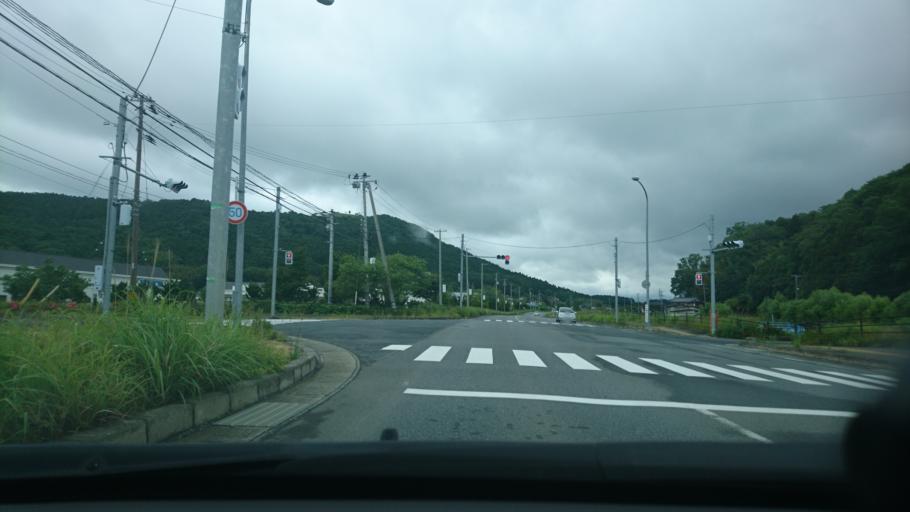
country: JP
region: Miyagi
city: Ishinomaki
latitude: 38.4594
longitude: 141.3098
